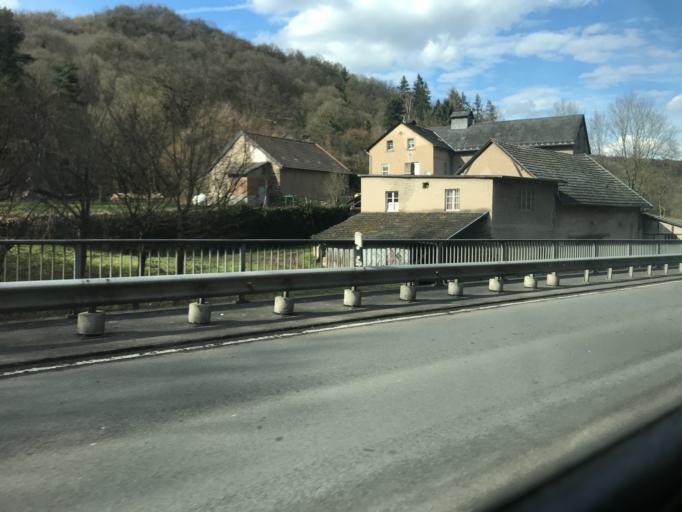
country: DE
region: Rheinland-Pfalz
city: Brohl-Lutzing
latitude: 50.4654
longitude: 7.3081
